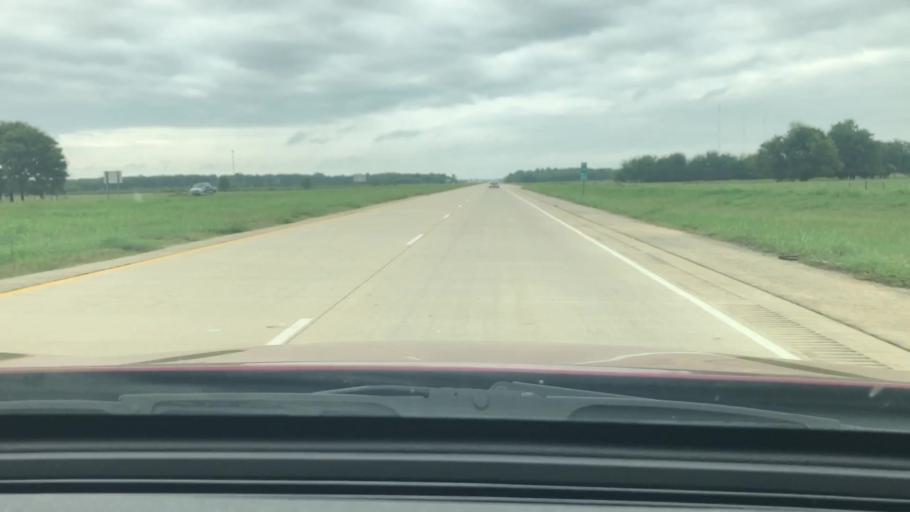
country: US
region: Louisiana
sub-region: Bossier Parish
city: Benton
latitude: 32.6987
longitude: -93.8602
